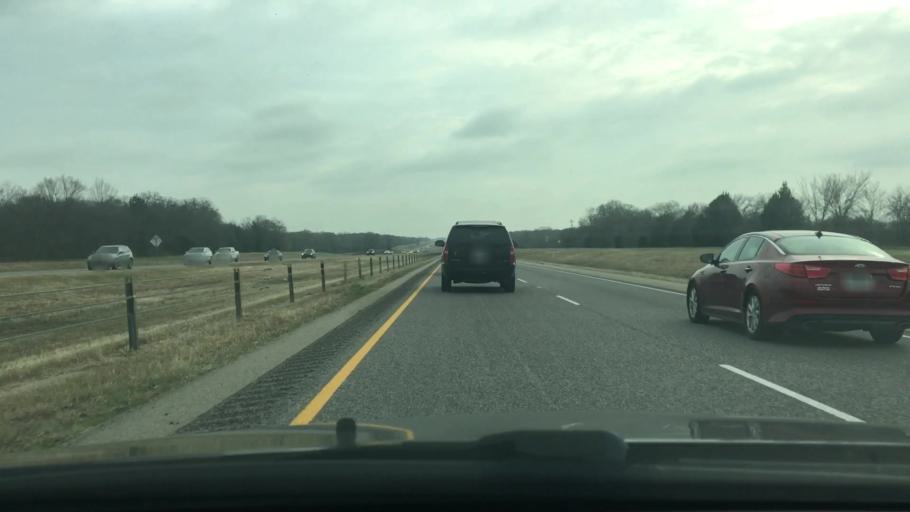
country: US
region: Texas
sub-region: Freestone County
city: Fairfield
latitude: 31.6328
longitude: -96.1581
